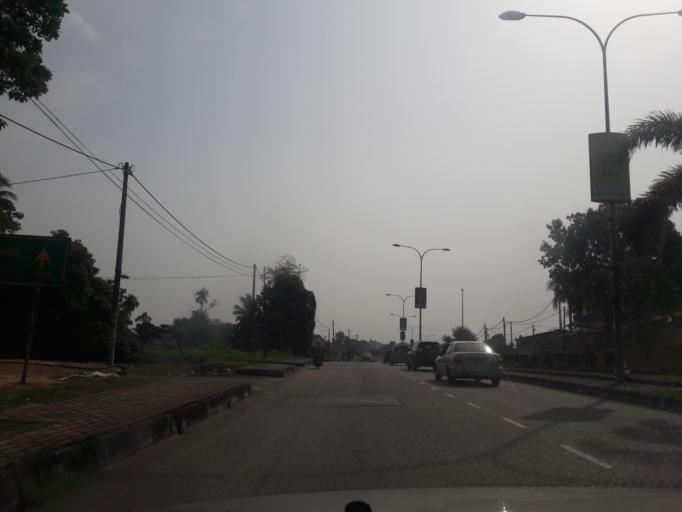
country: MY
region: Kedah
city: Kulim
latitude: 5.3601
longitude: 100.5453
